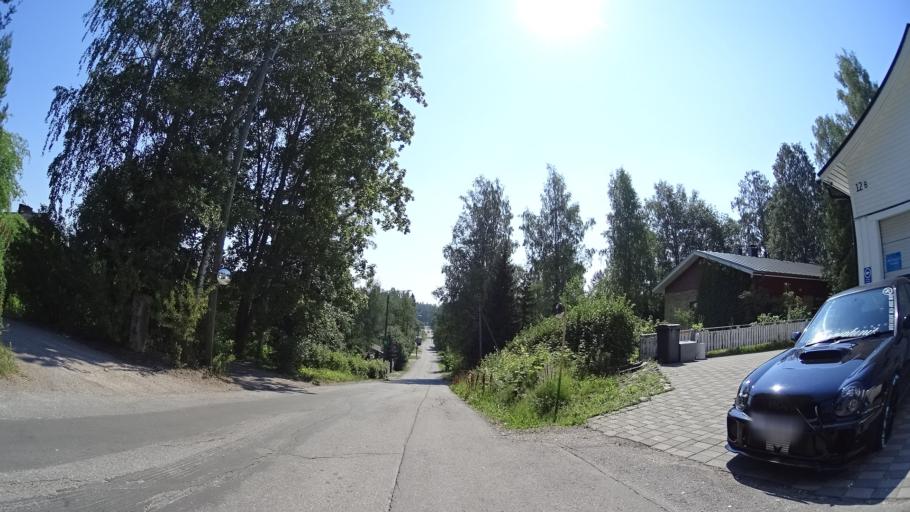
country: FI
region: Uusimaa
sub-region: Helsinki
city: Kerava
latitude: 60.3589
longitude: 25.0725
